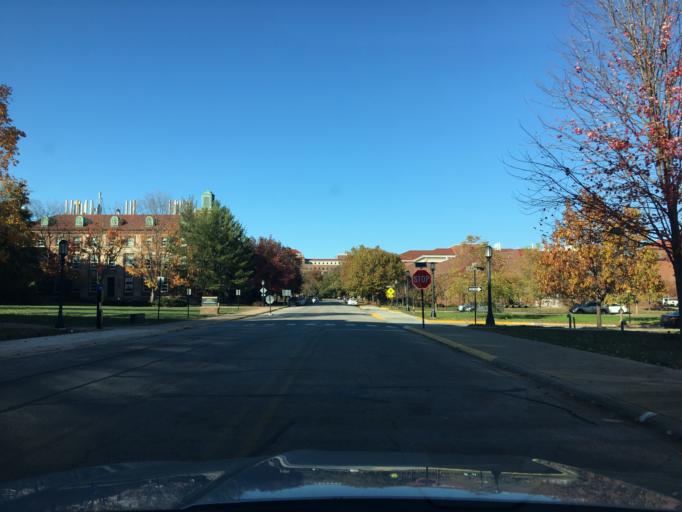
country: US
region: Indiana
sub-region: Tippecanoe County
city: West Lafayette
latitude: 40.4217
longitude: -86.9159
